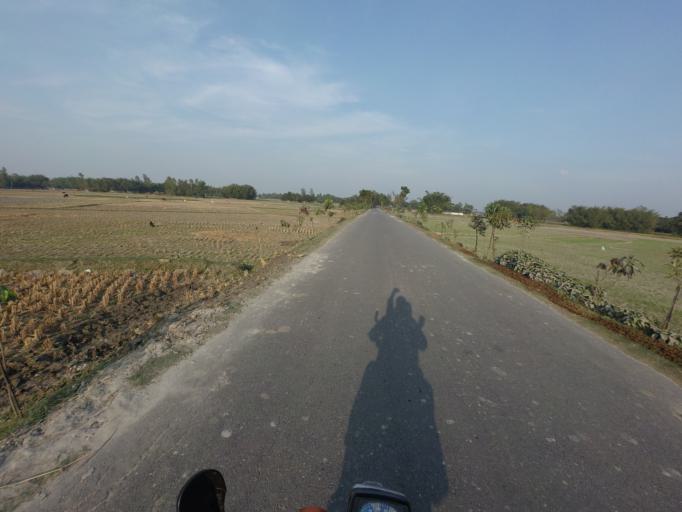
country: BD
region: Rajshahi
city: Saidpur
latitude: 25.9975
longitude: 88.7492
